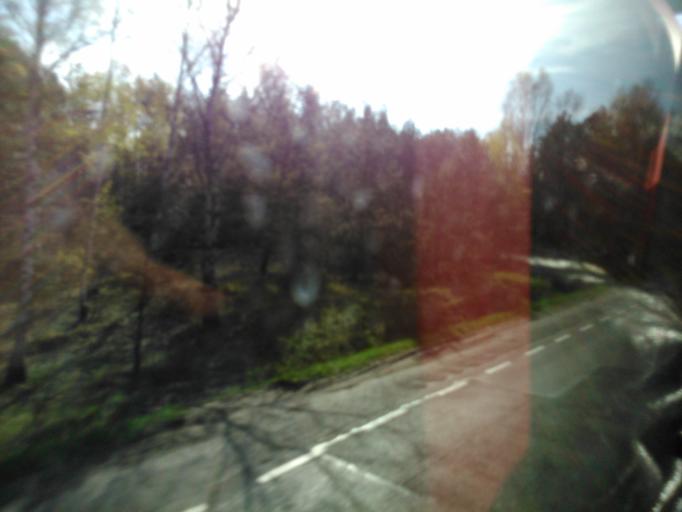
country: PL
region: Kujawsko-Pomorskie
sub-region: Torun
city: Torun
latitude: 52.9876
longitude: 18.6653
